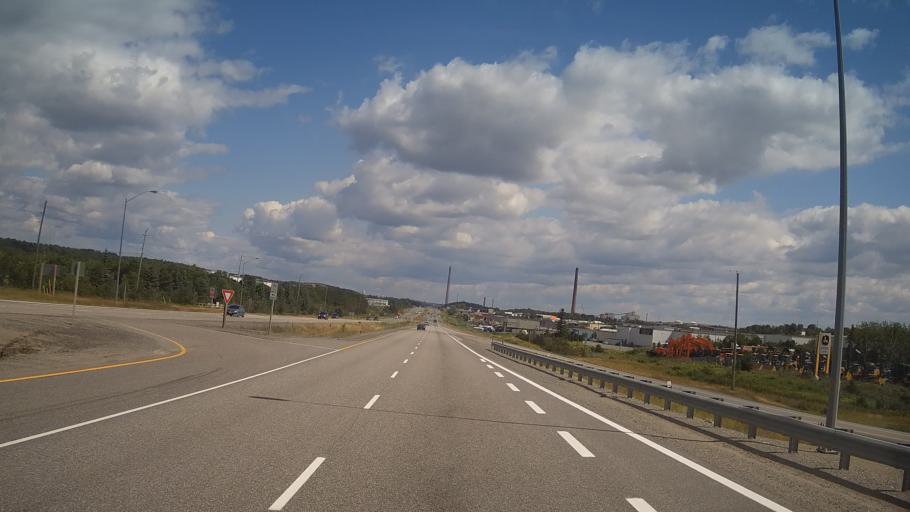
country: CA
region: Ontario
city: Greater Sudbury
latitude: 46.4288
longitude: -81.1191
